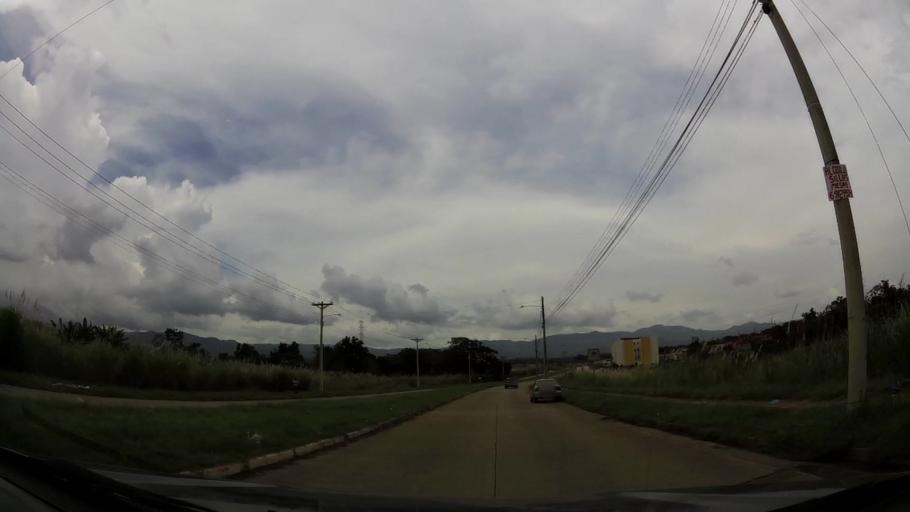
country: PA
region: Panama
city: Cabra Numero Uno
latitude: 9.1109
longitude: -79.3203
